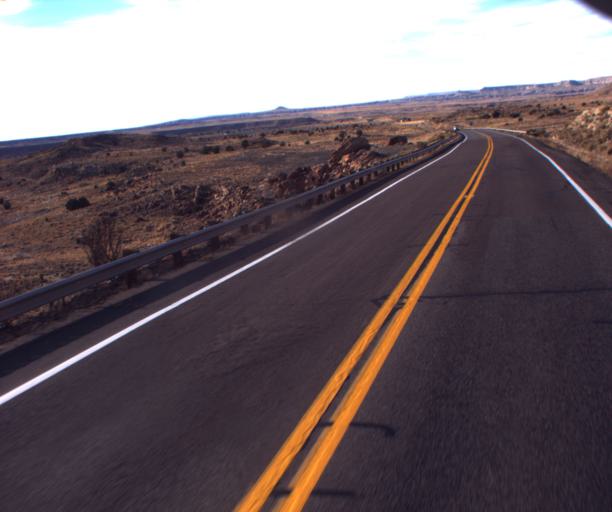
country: US
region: New Mexico
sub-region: San Juan County
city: Shiprock
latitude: 36.9136
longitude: -109.0753
